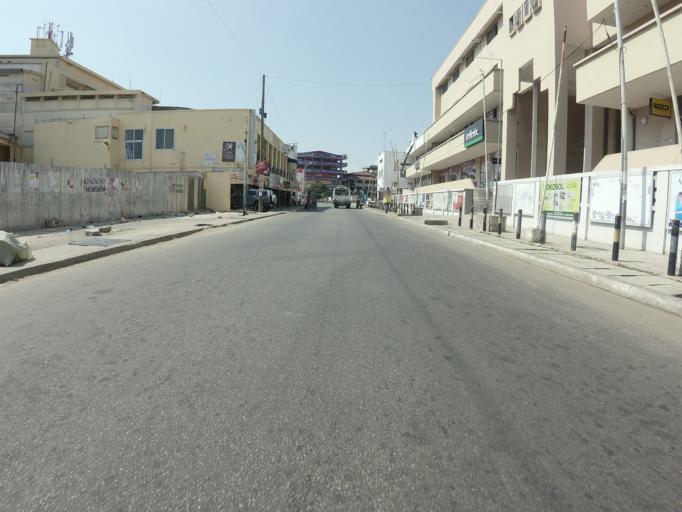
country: GH
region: Greater Accra
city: Accra
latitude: 5.5448
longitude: -0.2068
